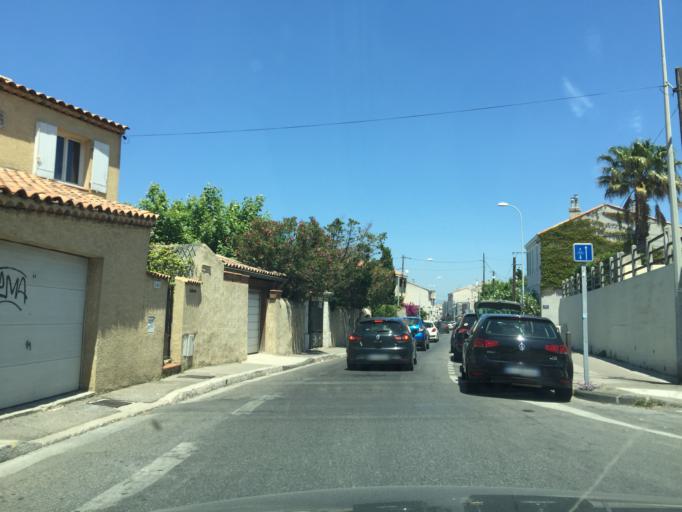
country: FR
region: Provence-Alpes-Cote d'Azur
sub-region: Departement des Bouches-du-Rhone
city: Marseille 08
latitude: 43.2420
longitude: 5.3689
